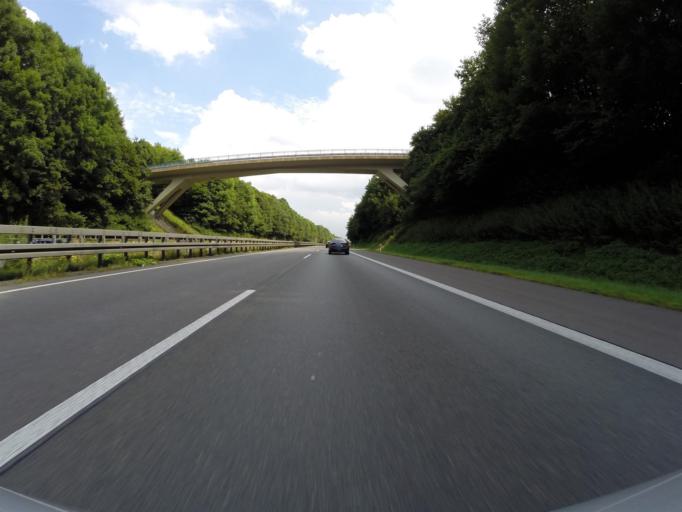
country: DE
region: North Rhine-Westphalia
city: Marsberg
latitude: 51.5236
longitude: 8.9170
